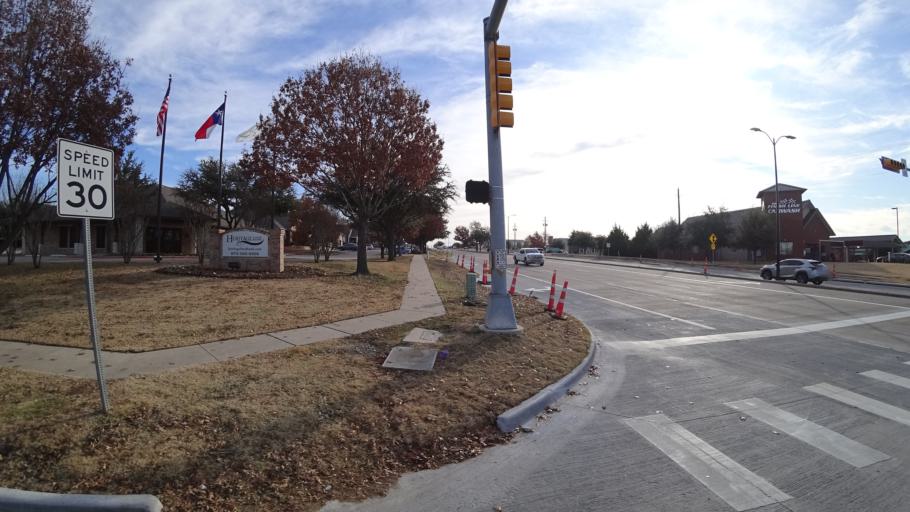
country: US
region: Texas
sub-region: Collin County
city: McKinney
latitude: 33.1990
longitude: -96.6549
